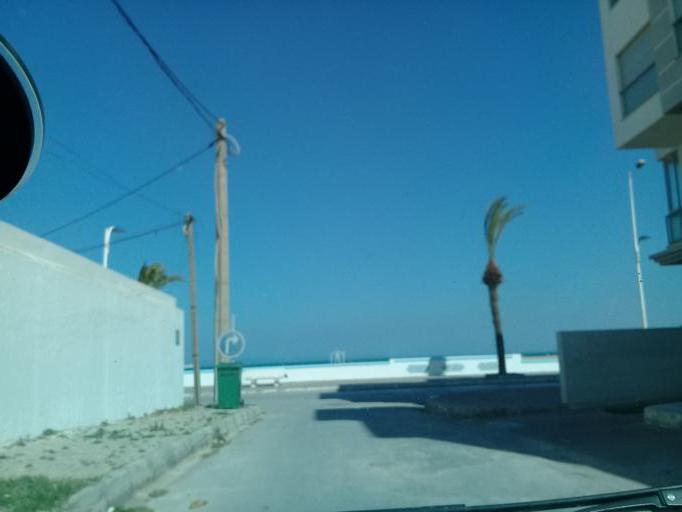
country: TN
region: Tunis
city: La Goulette
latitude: 36.8143
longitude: 10.3044
